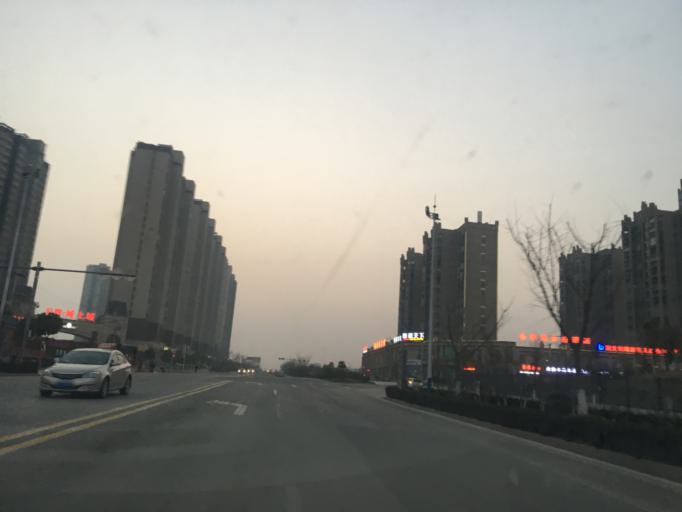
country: CN
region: Hubei
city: Nanhu
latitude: 31.1606
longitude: 115.0139
